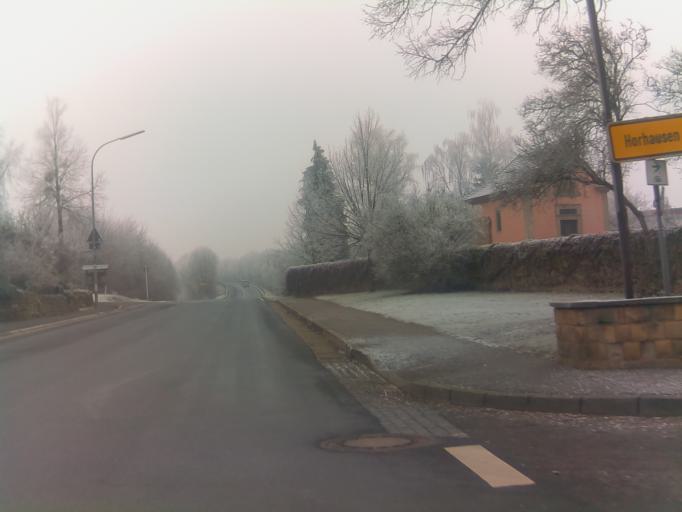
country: DE
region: Bavaria
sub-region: Regierungsbezirk Unterfranken
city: Wonfurt
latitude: 50.0097
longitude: 10.4651
